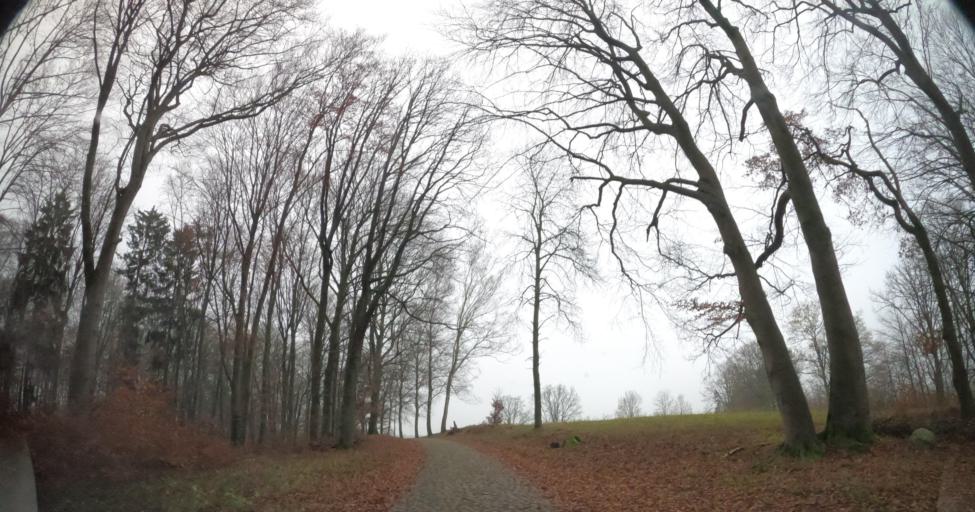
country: PL
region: West Pomeranian Voivodeship
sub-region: Powiat drawski
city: Drawsko Pomorskie
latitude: 53.5552
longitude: 15.7232
